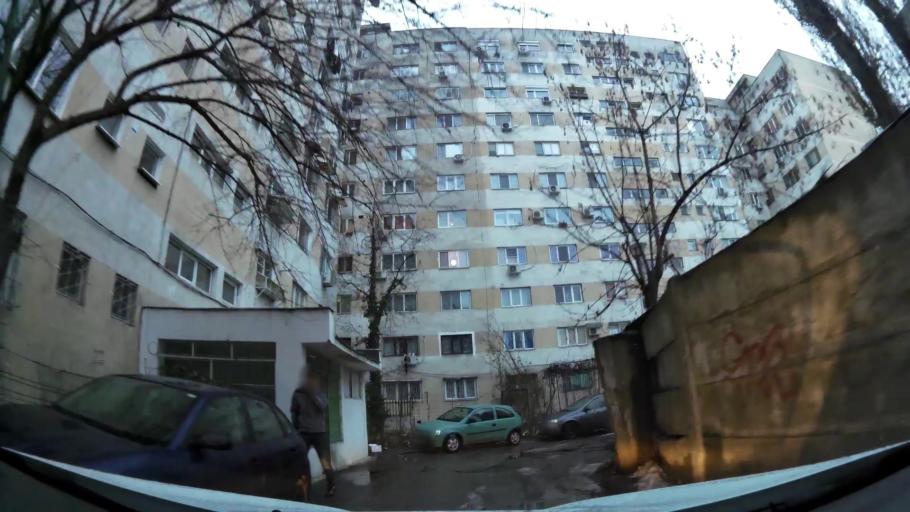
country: RO
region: Ilfov
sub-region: Comuna Chiajna
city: Rosu
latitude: 44.4337
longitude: 26.0242
